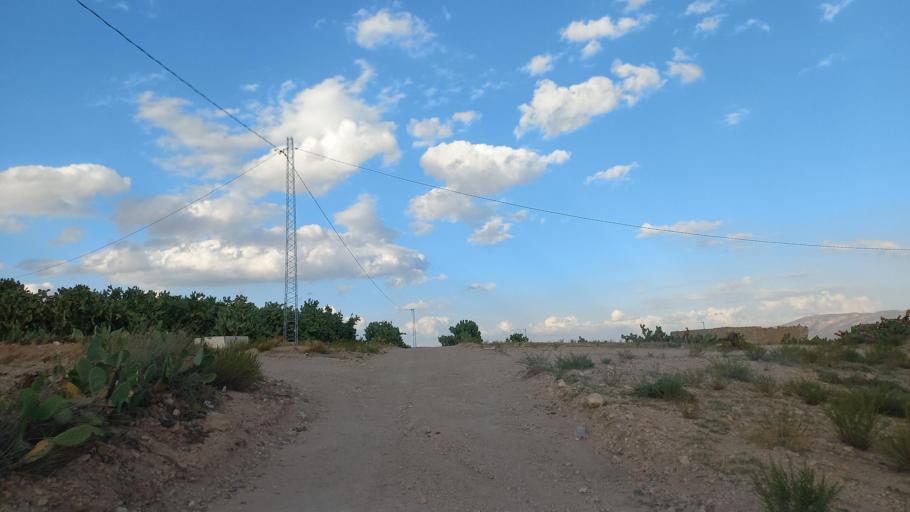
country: TN
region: Al Qasrayn
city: Sbiba
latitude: 35.3898
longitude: 9.0462
